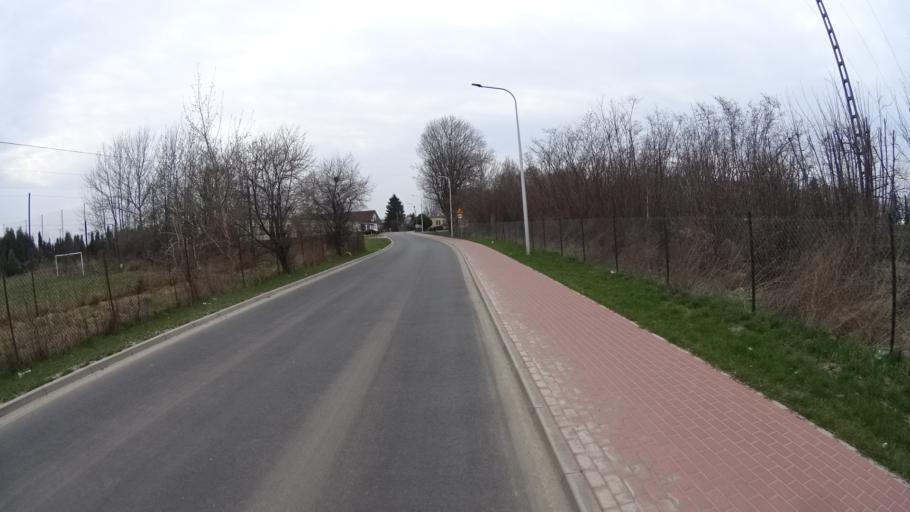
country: PL
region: Masovian Voivodeship
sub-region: Powiat pruszkowski
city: Piastow
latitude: 52.2108
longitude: 20.8458
